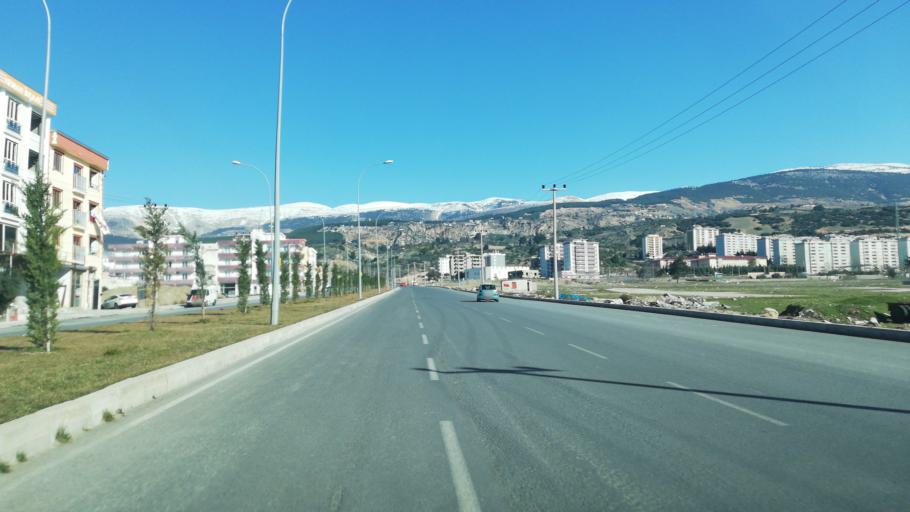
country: TR
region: Kahramanmaras
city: Kahramanmaras
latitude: 37.5783
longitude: 36.9746
